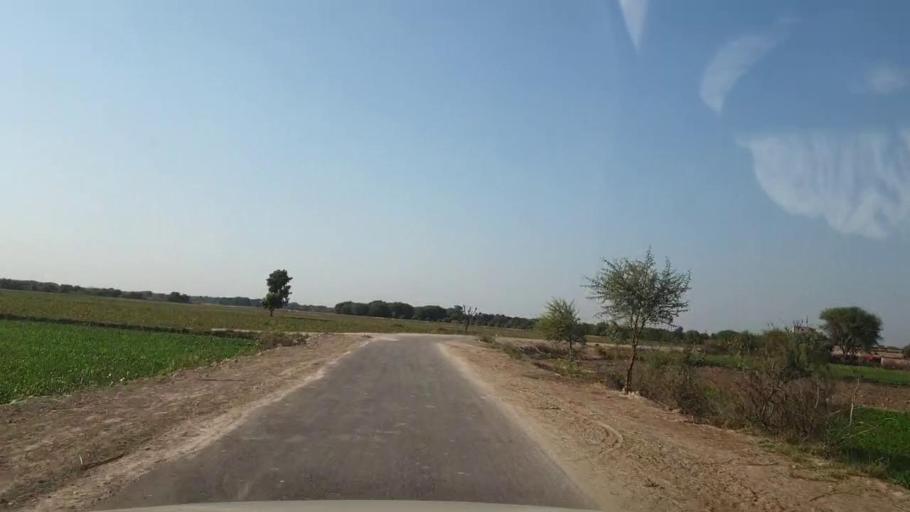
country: PK
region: Sindh
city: Tando Allahyar
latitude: 25.4860
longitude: 68.6570
